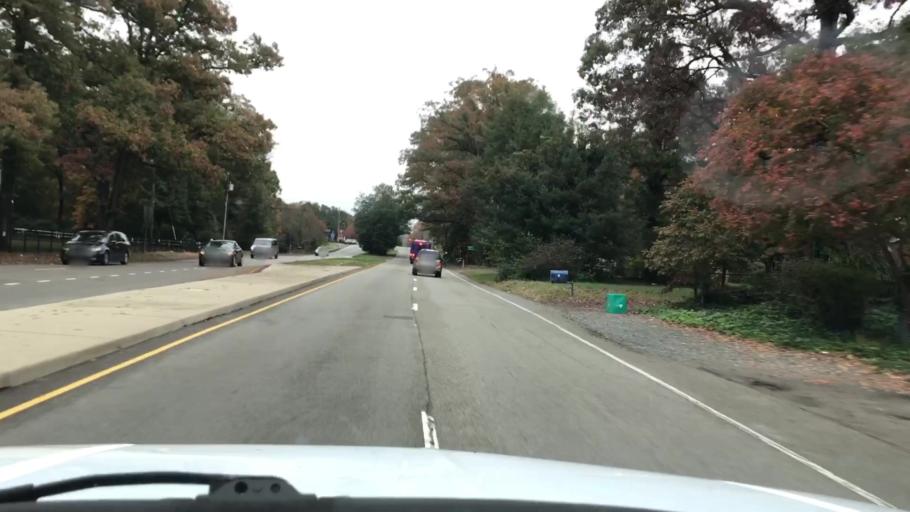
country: US
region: Virginia
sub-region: Henrico County
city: Lakeside
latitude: 37.6064
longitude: -77.4495
